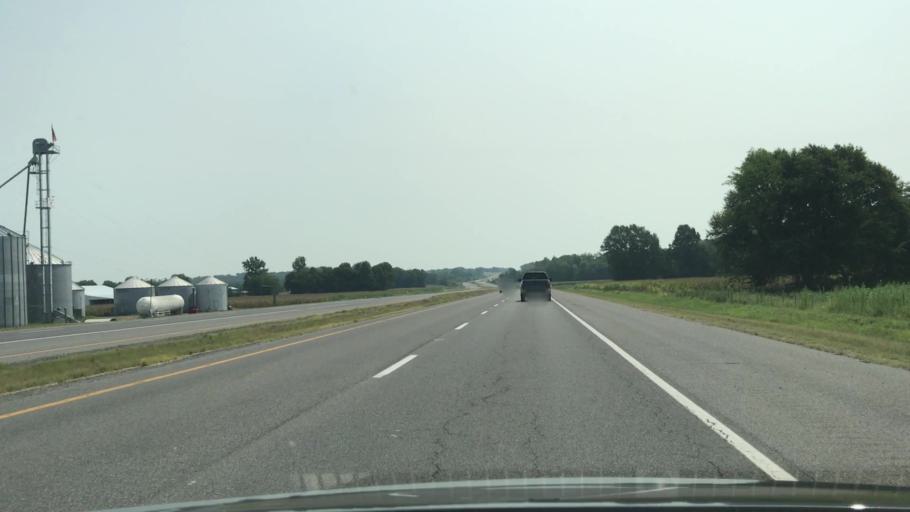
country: US
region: Kentucky
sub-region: Calloway County
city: Murray
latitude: 36.6518
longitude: -88.3005
